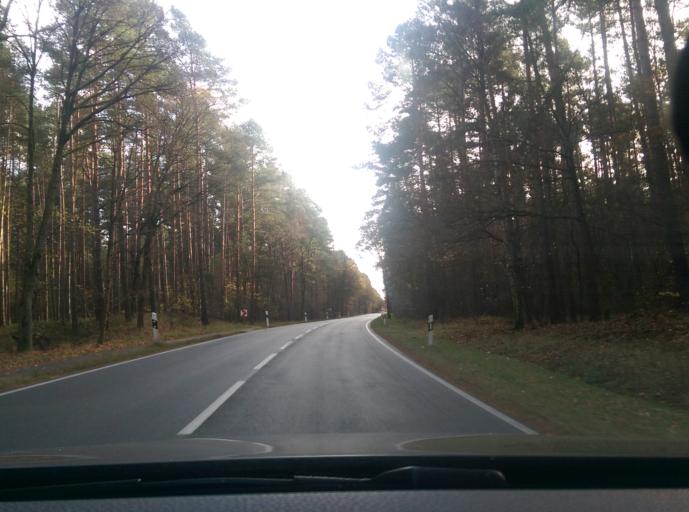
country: DE
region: Lower Saxony
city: Hambuhren
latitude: 52.6666
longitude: 9.9754
